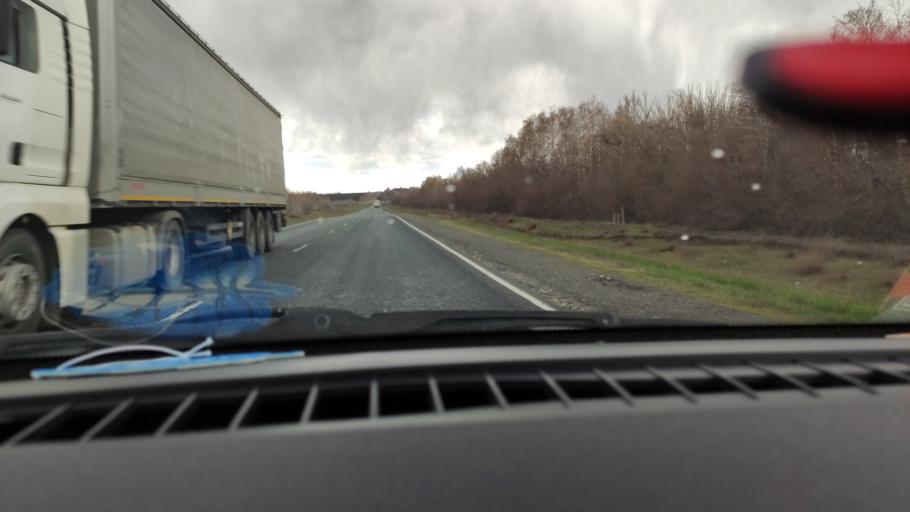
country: RU
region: Saratov
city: Balakovo
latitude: 52.1411
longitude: 47.8011
